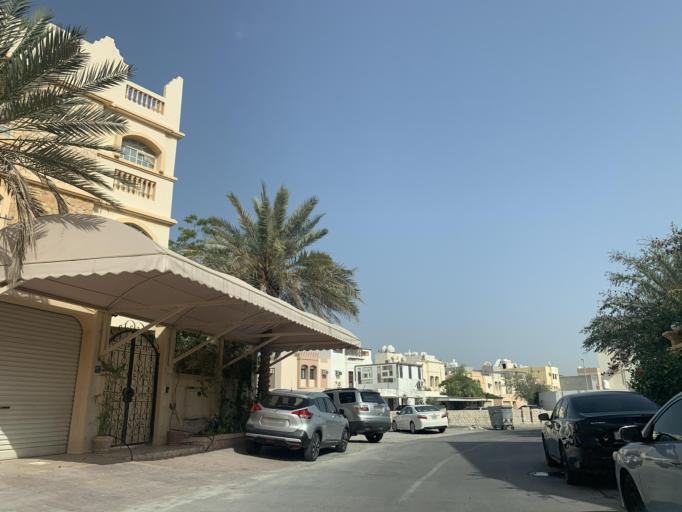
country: BH
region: Muharraq
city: Al Muharraq
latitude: 26.2759
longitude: 50.6089
